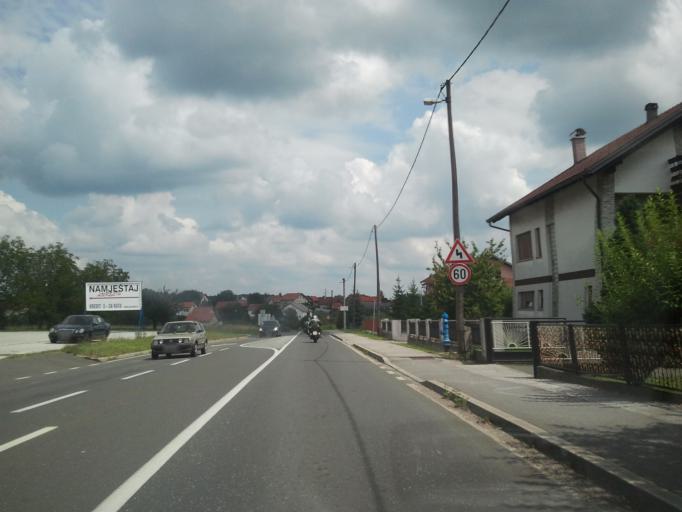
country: HR
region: Grad Zagreb
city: Horvati
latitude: 45.6923
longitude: 15.7441
